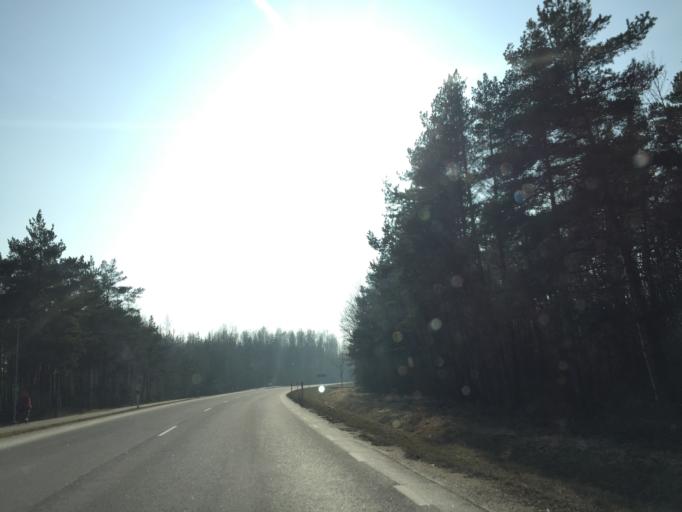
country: EE
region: Saare
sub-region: Kuressaare linn
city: Kuressaare
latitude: 58.2424
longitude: 22.4508
